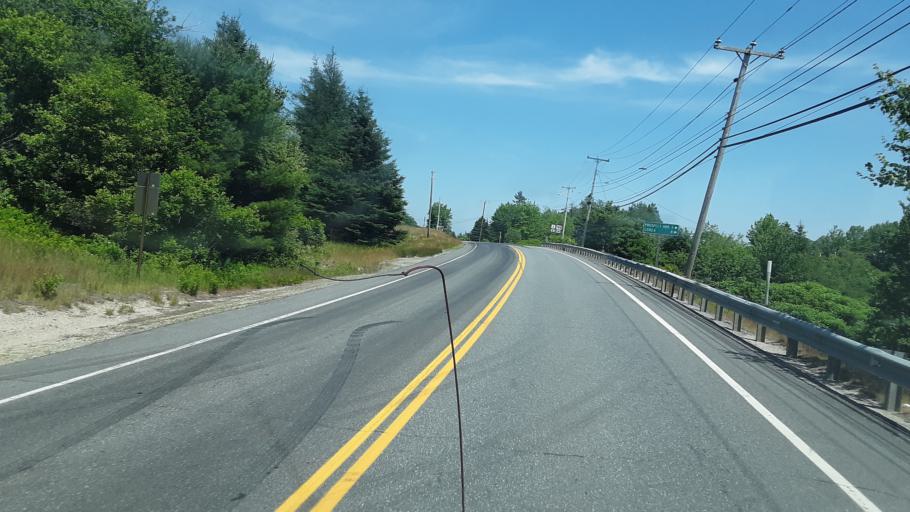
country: US
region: Maine
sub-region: Hancock County
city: Gouldsboro
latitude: 44.4685
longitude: -68.0762
